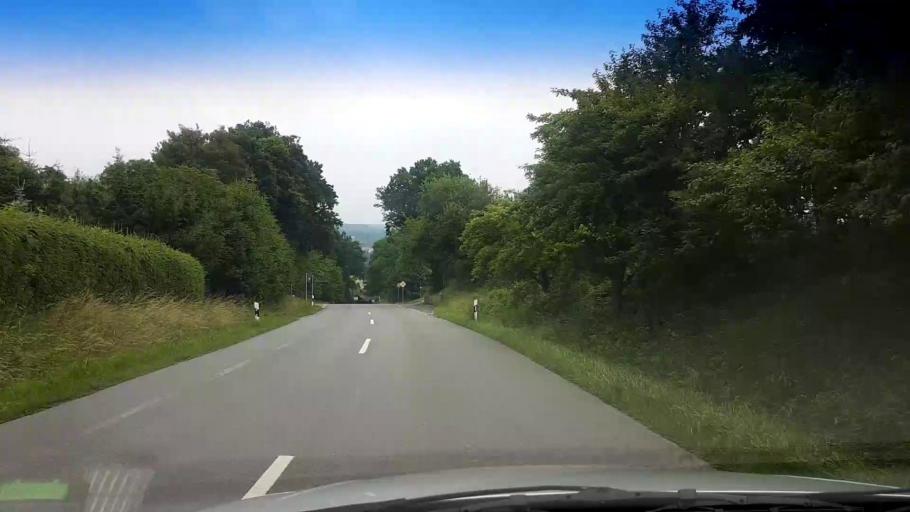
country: DE
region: Bavaria
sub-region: Upper Franconia
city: Mainleus
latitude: 50.0940
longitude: 11.3571
